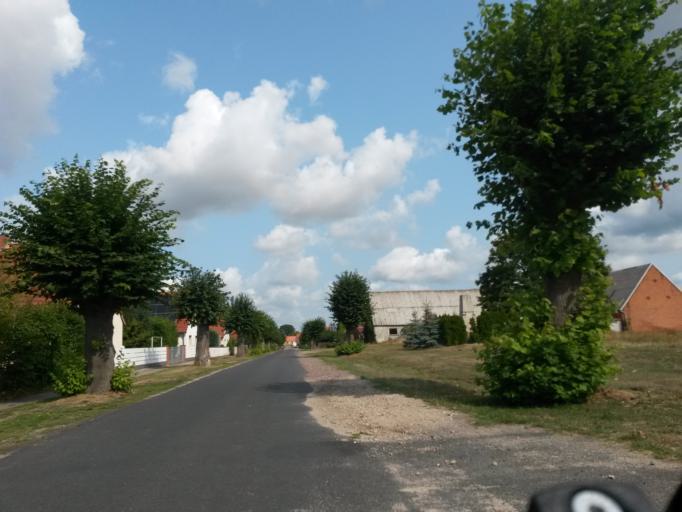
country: DE
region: Saxony-Anhalt
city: Klietz
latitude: 52.6494
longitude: 12.0418
